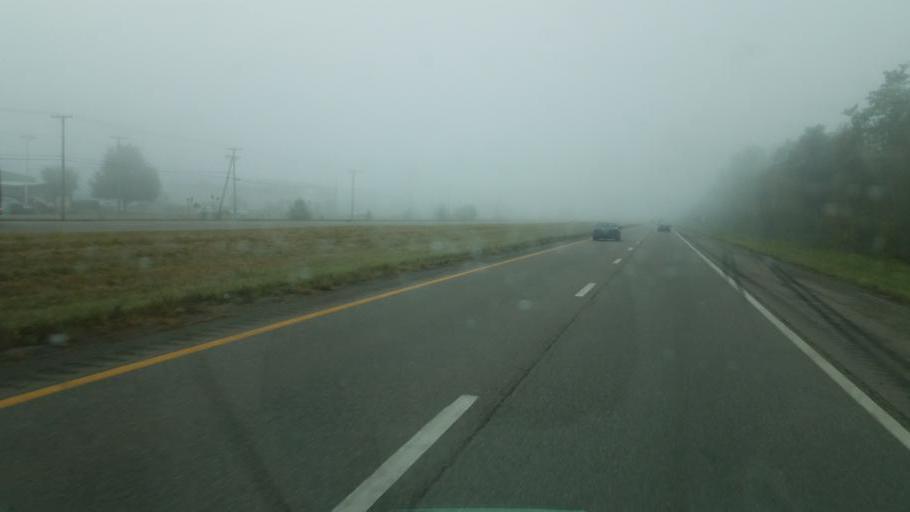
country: US
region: Ohio
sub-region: Tuscarawas County
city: Dover
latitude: 40.5217
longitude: -81.4906
